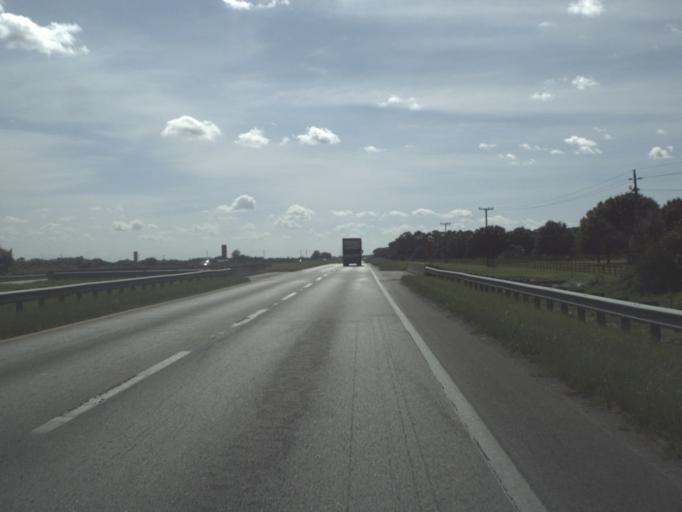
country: US
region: Florida
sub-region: Hendry County
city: LaBelle
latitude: 26.7383
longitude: -81.4705
